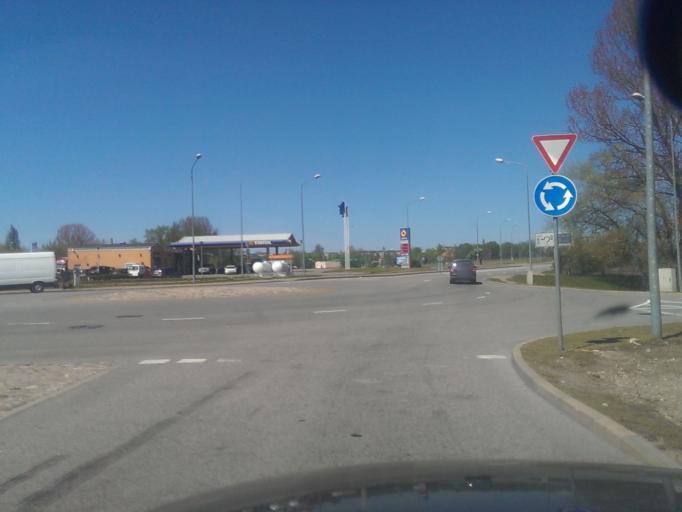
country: LV
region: Ventspils
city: Ventspils
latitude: 57.3845
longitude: 21.5877
